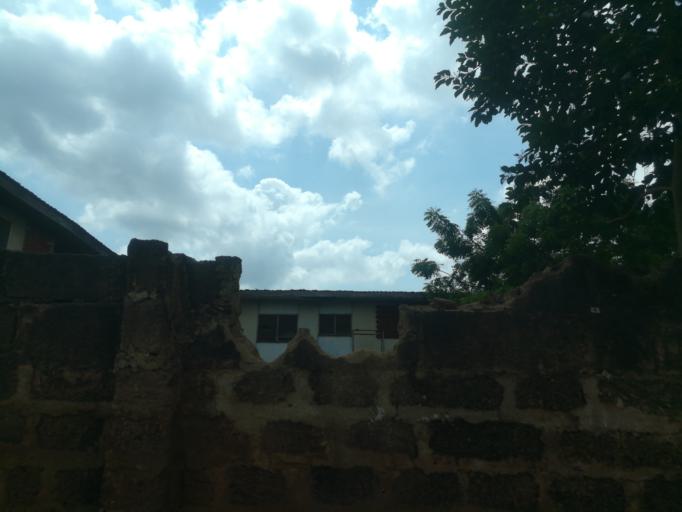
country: NG
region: Oyo
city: Ibadan
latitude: 7.4097
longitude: 3.9416
